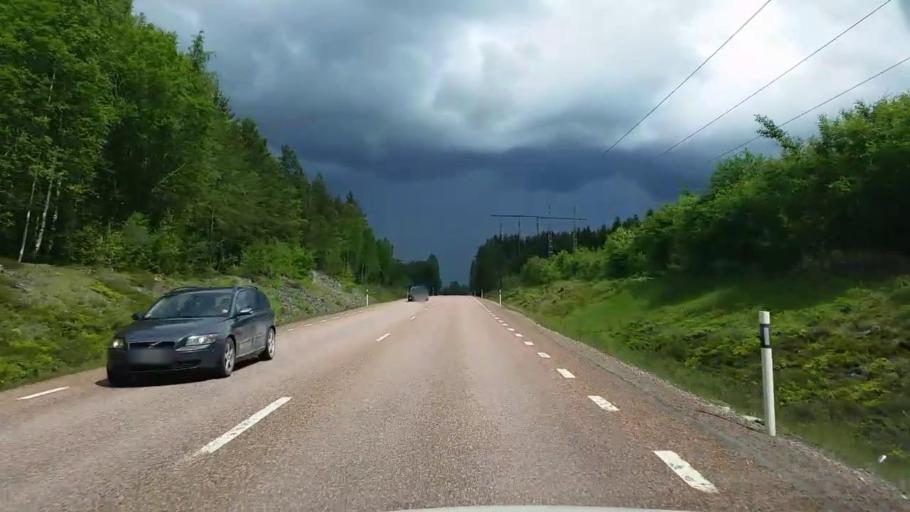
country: SE
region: Gaevleborg
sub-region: Hofors Kommun
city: Hofors
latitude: 60.5437
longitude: 16.4673
